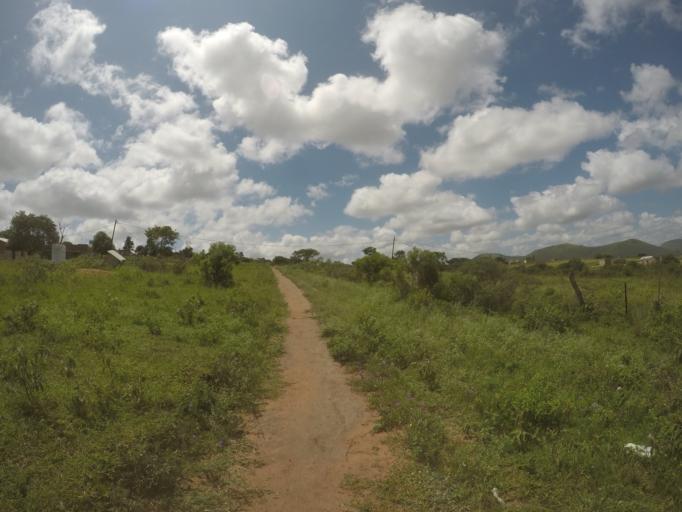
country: ZA
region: KwaZulu-Natal
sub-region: uThungulu District Municipality
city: Empangeni
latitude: -28.5823
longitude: 31.8406
